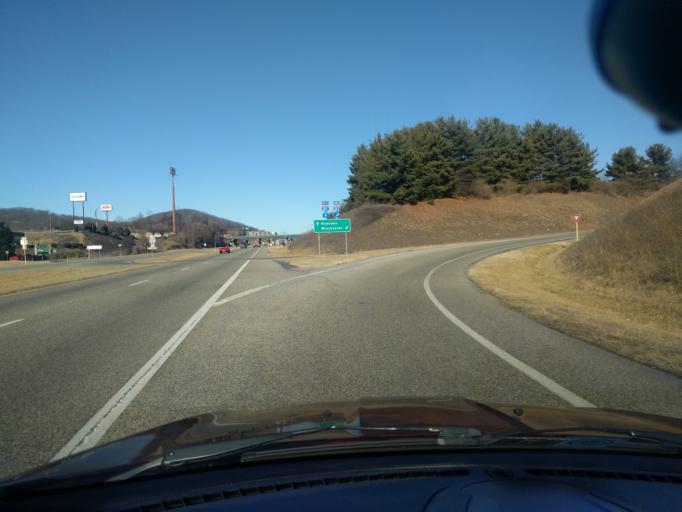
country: US
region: Virginia
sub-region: Augusta County
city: Jolivue
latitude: 38.1262
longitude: -79.0332
